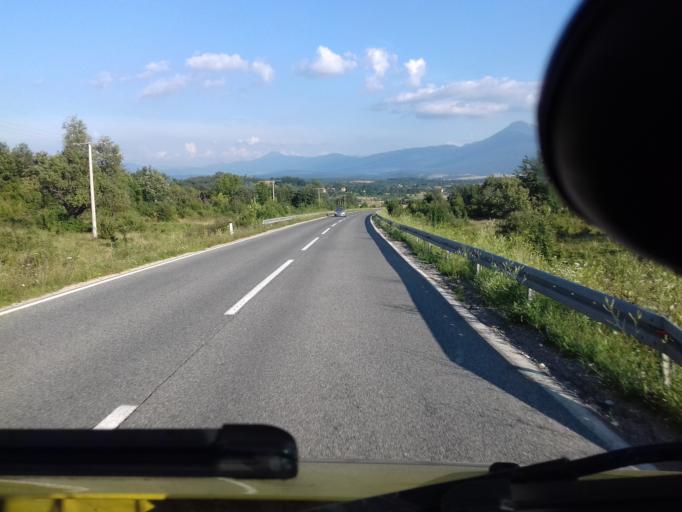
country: BA
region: Federation of Bosnia and Herzegovina
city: Orasac
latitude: 44.6500
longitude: 16.1621
